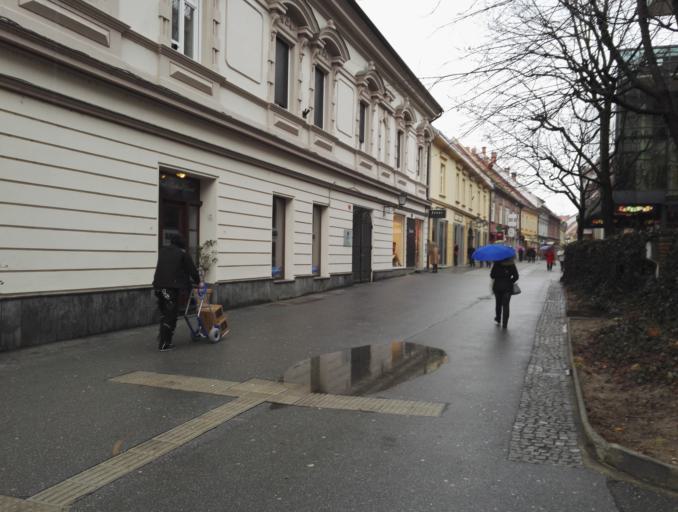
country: SI
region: Maribor
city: Maribor
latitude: 46.5577
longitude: 15.6462
